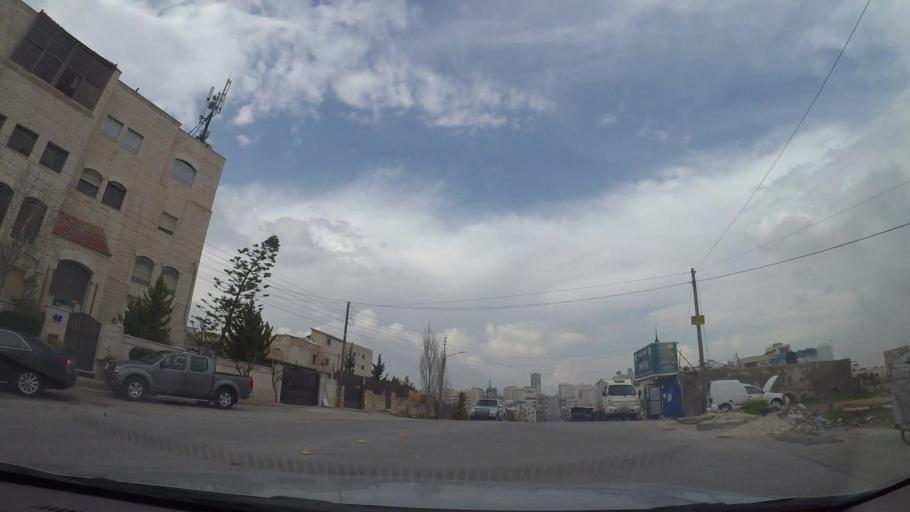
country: JO
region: Amman
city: Umm as Summaq
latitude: 31.8816
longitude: 35.8594
